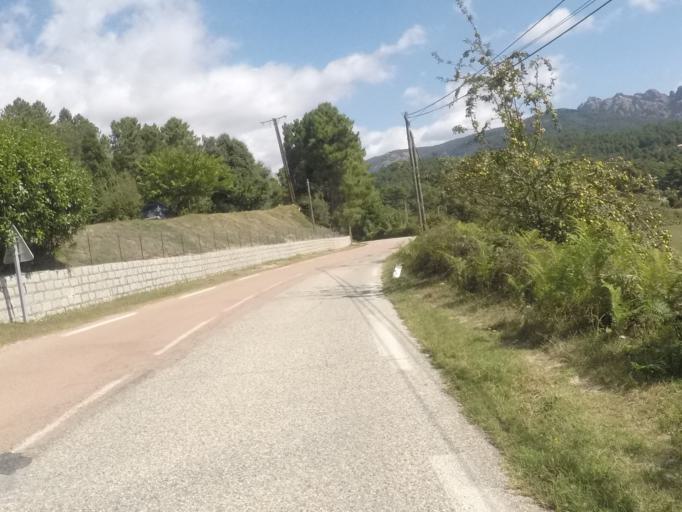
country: FR
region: Corsica
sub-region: Departement de la Corse-du-Sud
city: Zonza
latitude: 41.7579
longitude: 9.1822
